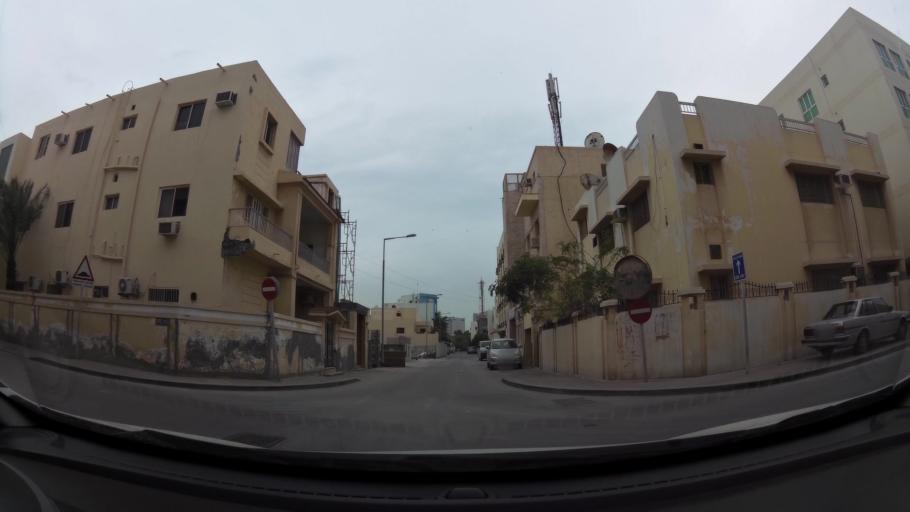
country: BH
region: Manama
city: Jidd Hafs
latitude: 26.2211
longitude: 50.5651
